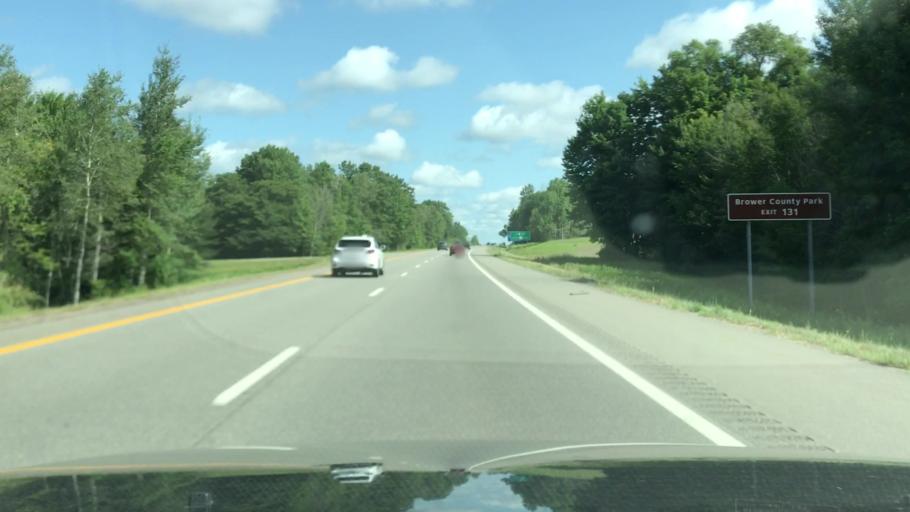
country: US
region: Michigan
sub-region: Mecosta County
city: Big Rapids
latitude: 43.5704
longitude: -85.4909
